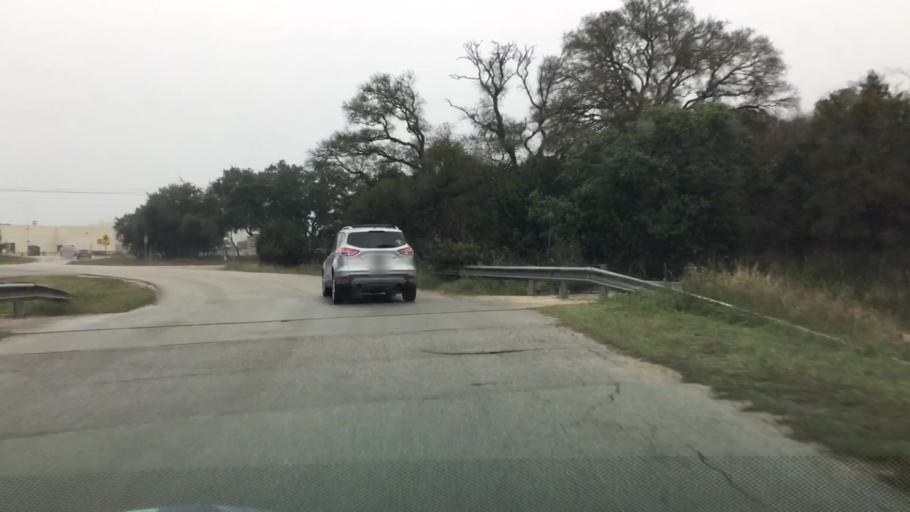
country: US
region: Texas
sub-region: Hays County
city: Dripping Springs
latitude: 30.1968
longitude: -98.0981
